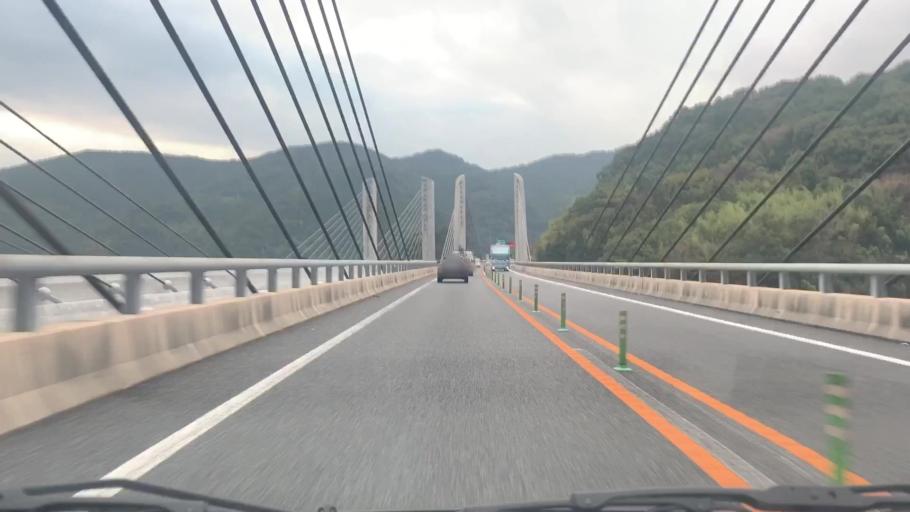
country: JP
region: Nagasaki
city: Nagasaki-shi
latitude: 32.7582
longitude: 129.9290
